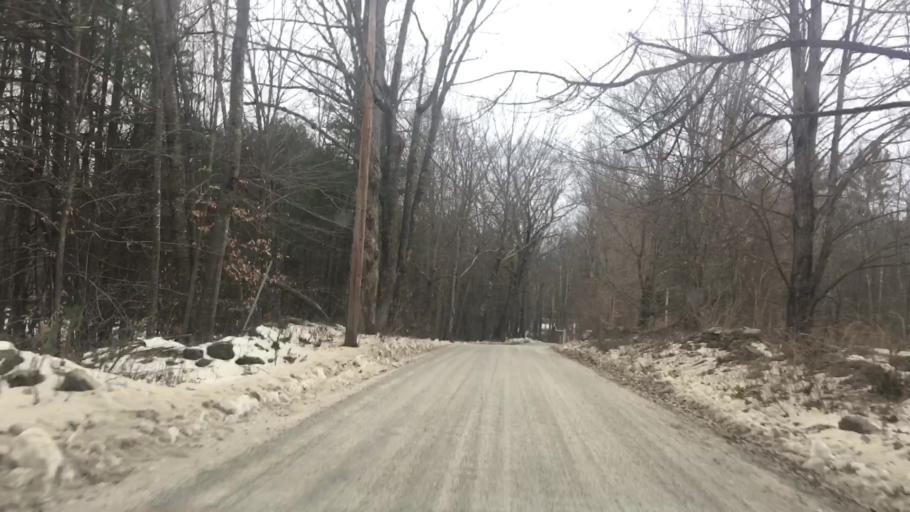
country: US
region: New Hampshire
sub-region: Merrimack County
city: Hopkinton
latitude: 43.1650
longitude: -71.6687
